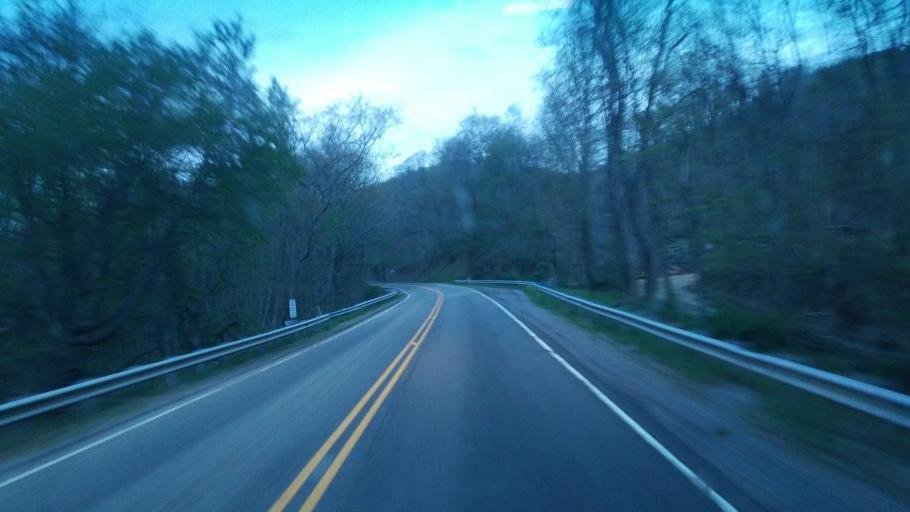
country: US
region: Virginia
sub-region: Smyth County
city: Atkins
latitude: 36.8177
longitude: -81.4381
